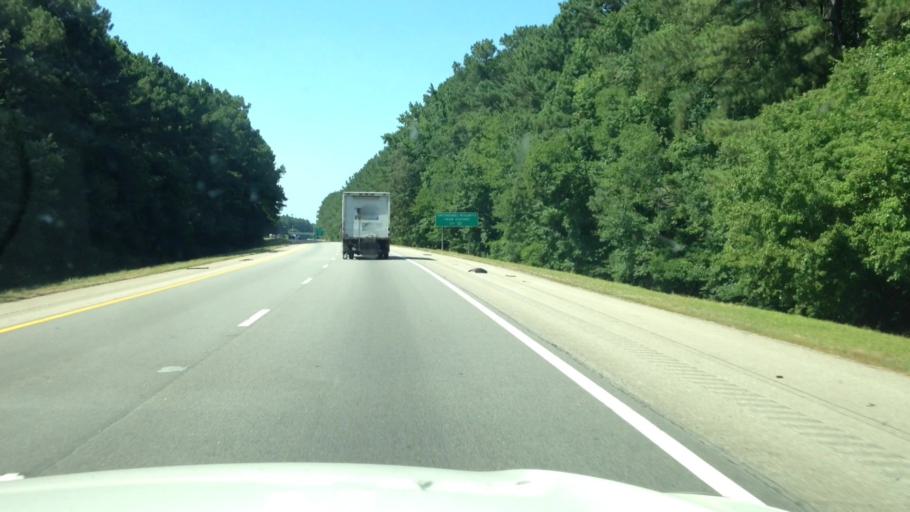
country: US
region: North Carolina
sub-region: Wilson County
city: Wilson
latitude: 35.7536
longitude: -78.0035
